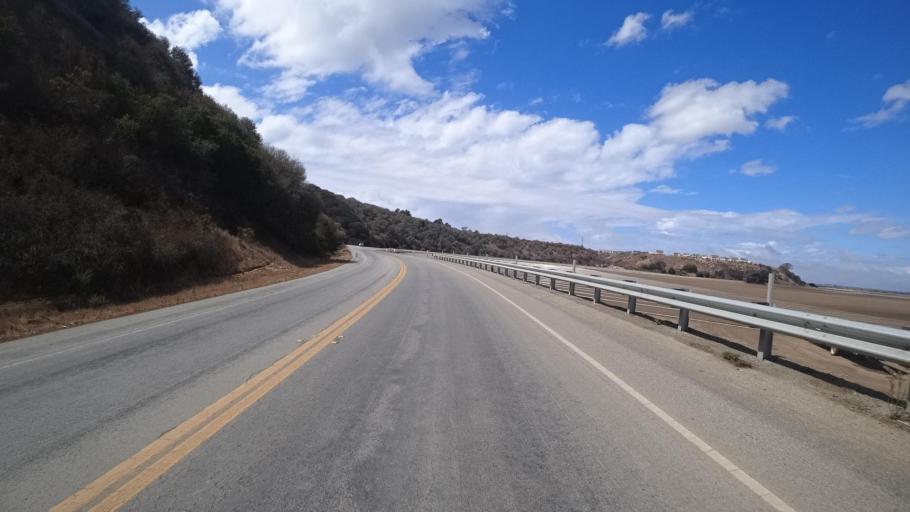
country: US
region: California
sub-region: Monterey County
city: Boronda
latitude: 36.6475
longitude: -121.7213
